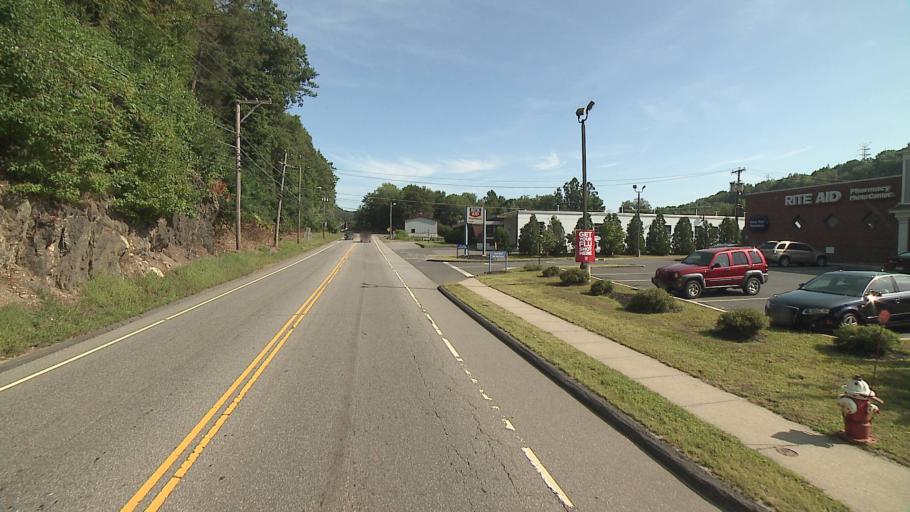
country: US
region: Connecticut
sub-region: Litchfield County
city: Thomaston
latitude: 41.6625
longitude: -73.0797
